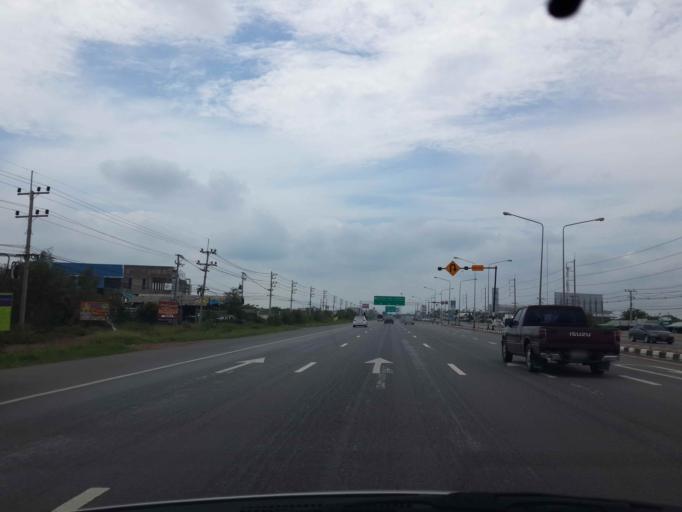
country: TH
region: Samut Songkhram
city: Samut Songkhram
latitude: 13.4094
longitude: 100.0211
